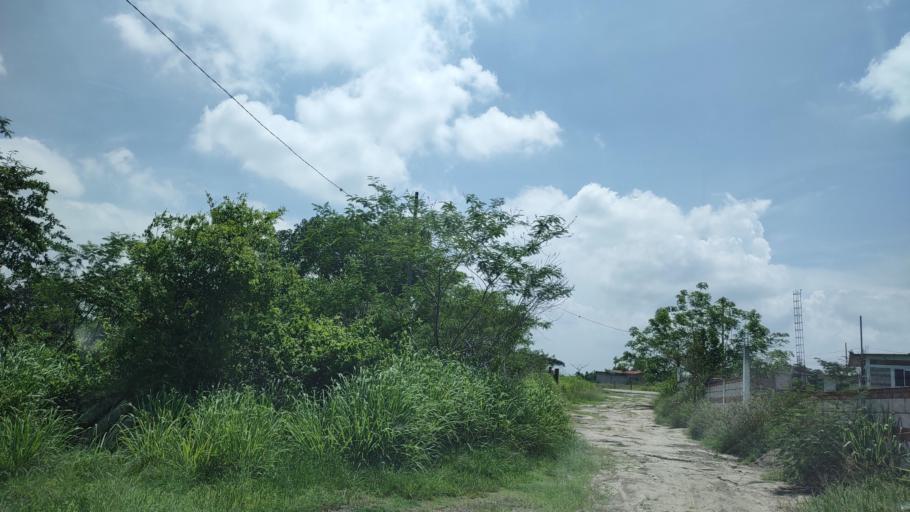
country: MX
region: Veracruz
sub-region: Emiliano Zapata
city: Dos Rios
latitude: 19.4264
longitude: -96.8042
